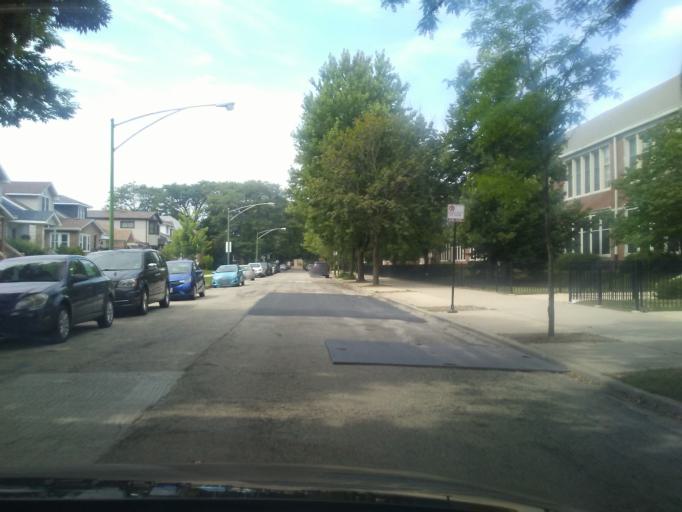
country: US
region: Illinois
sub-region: Cook County
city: Harwood Heights
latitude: 41.9835
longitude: -87.7792
